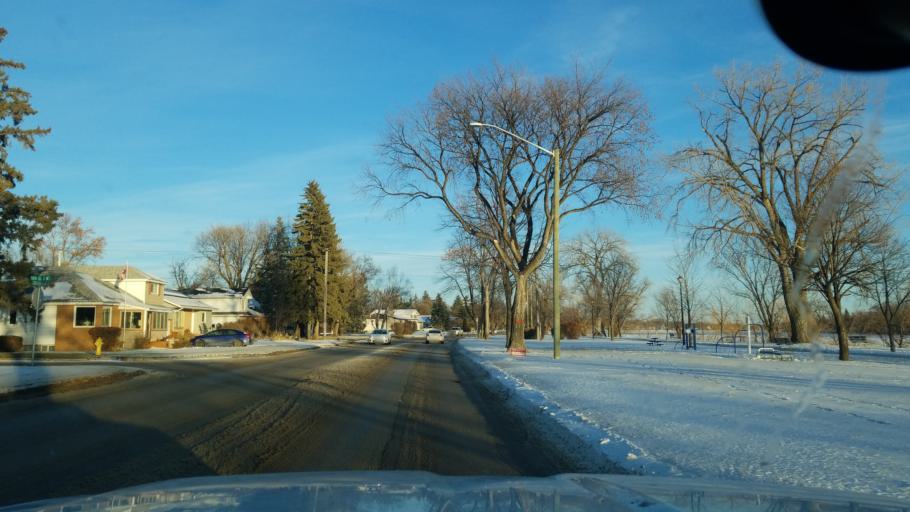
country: CA
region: Manitoba
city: Portage la Prairie
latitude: 49.9701
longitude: -98.3102
